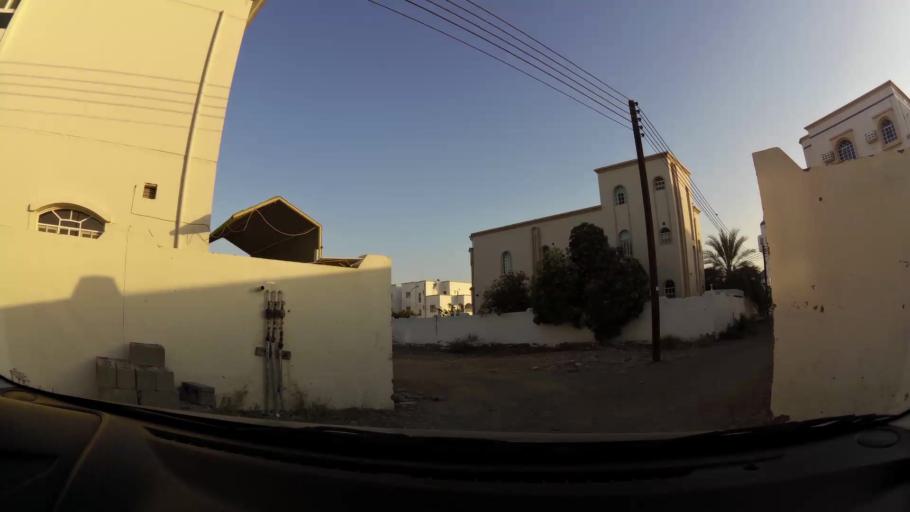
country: OM
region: Muhafazat Masqat
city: As Sib al Jadidah
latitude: 23.6124
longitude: 58.2015
